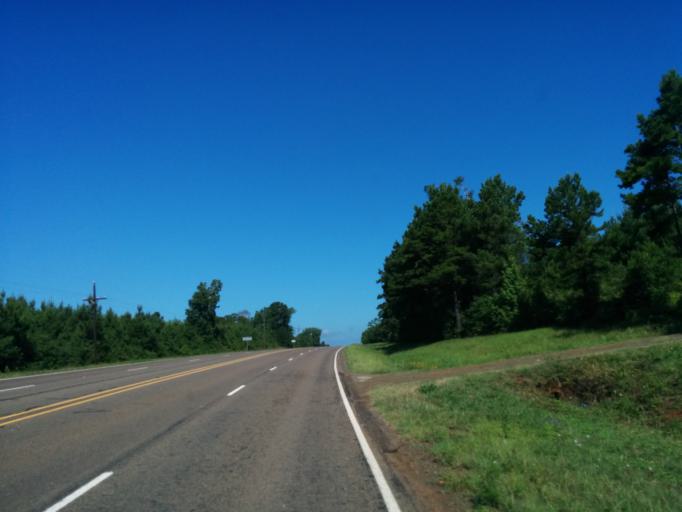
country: US
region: Texas
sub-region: Sabine County
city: Milam
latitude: 31.4312
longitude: -93.8250
